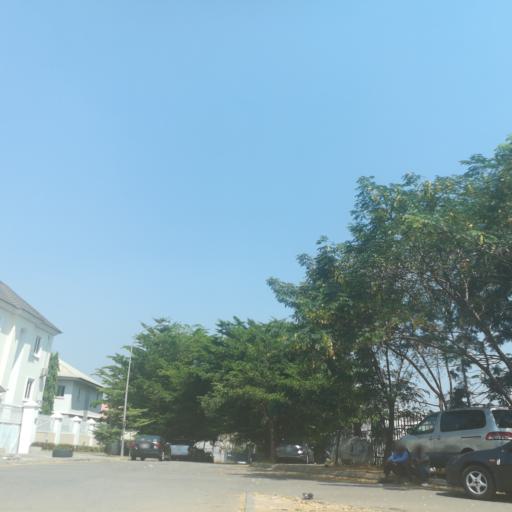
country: NG
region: Abuja Federal Capital Territory
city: Abuja
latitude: 9.0740
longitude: 7.4498
